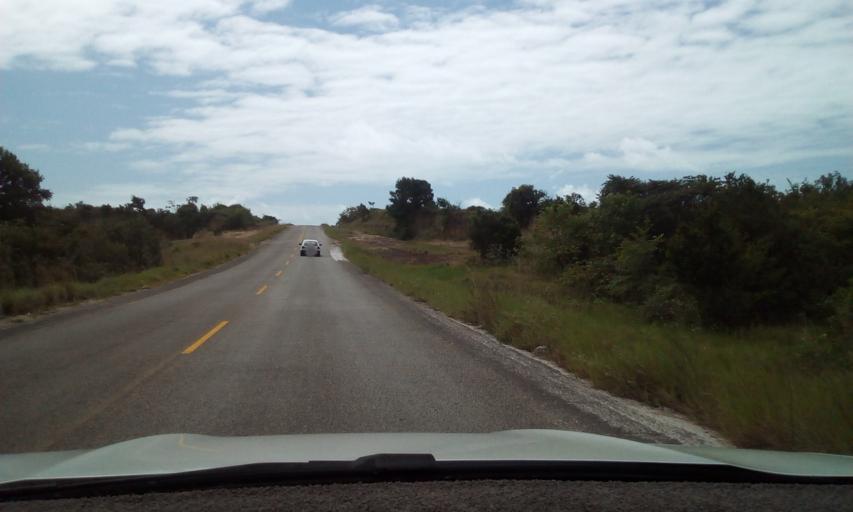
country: BR
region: Paraiba
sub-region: Rio Tinto
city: Rio Tinto
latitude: -6.7324
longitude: -34.9601
